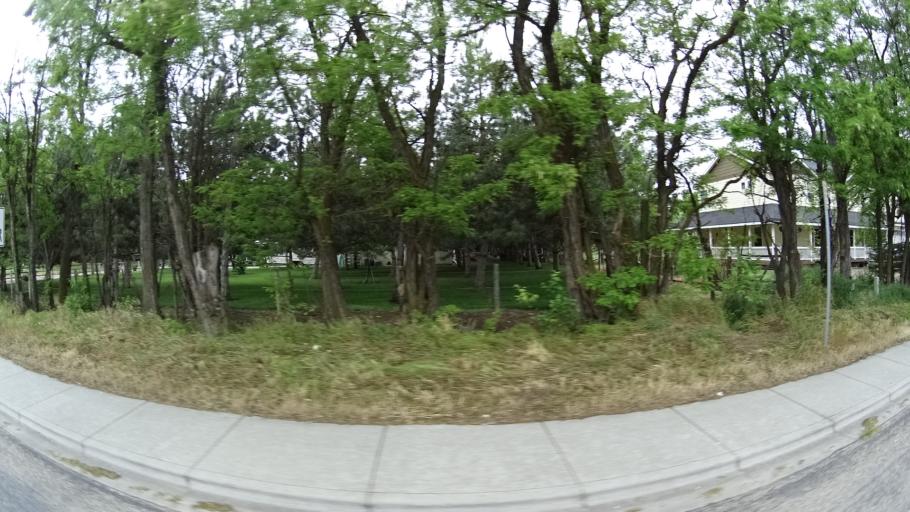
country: US
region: Idaho
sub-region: Ada County
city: Eagle
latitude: 43.7065
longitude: -116.3658
